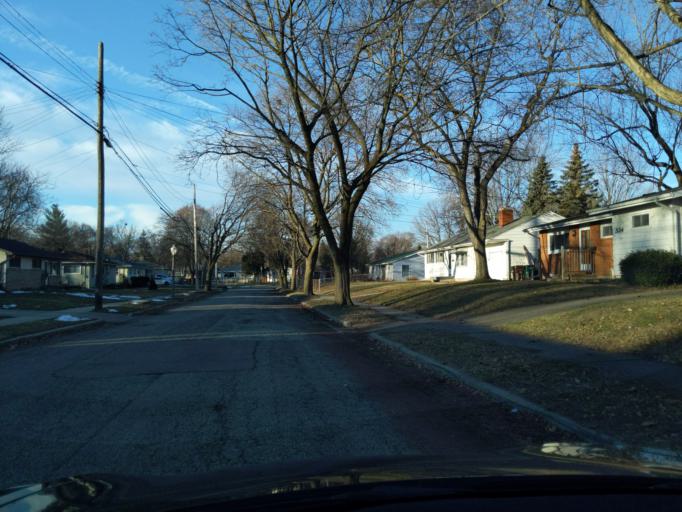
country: US
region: Michigan
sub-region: Ingham County
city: Lansing
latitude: 42.6950
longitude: -84.5596
